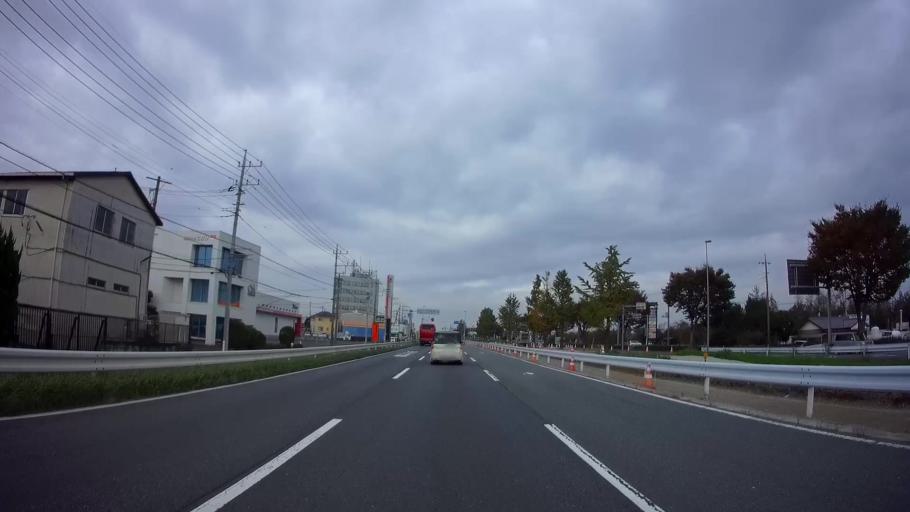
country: JP
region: Saitama
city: Kumagaya
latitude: 36.1576
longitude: 139.4080
